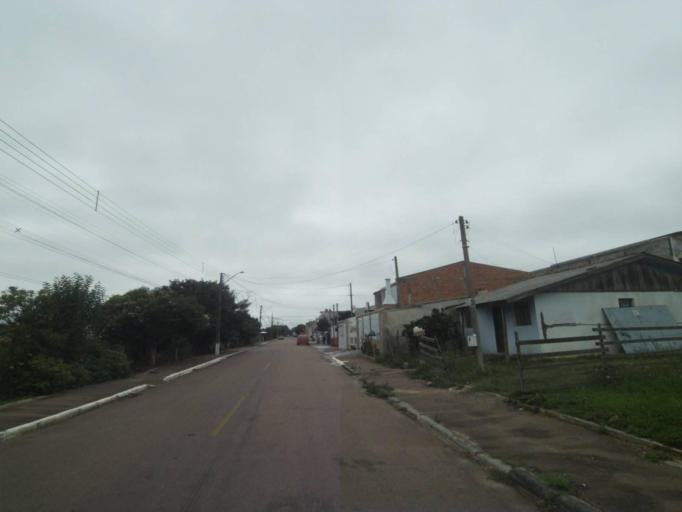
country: BR
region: Parana
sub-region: Araucaria
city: Araucaria
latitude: -25.5442
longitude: -49.3447
